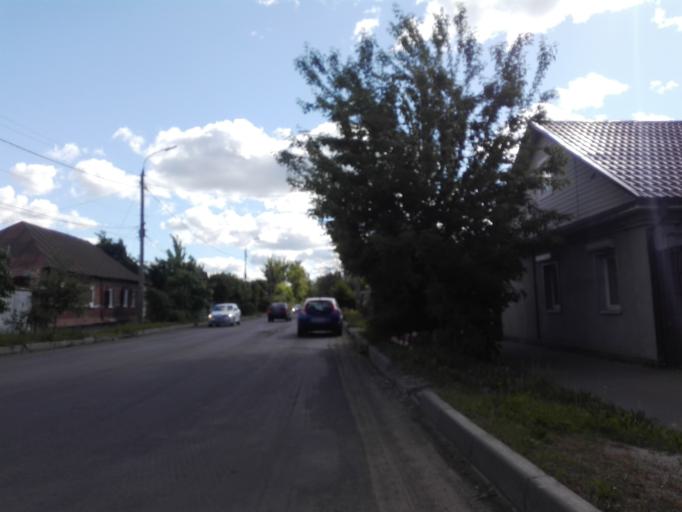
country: RU
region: Orjol
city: Orel
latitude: 52.9555
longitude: 36.0509
